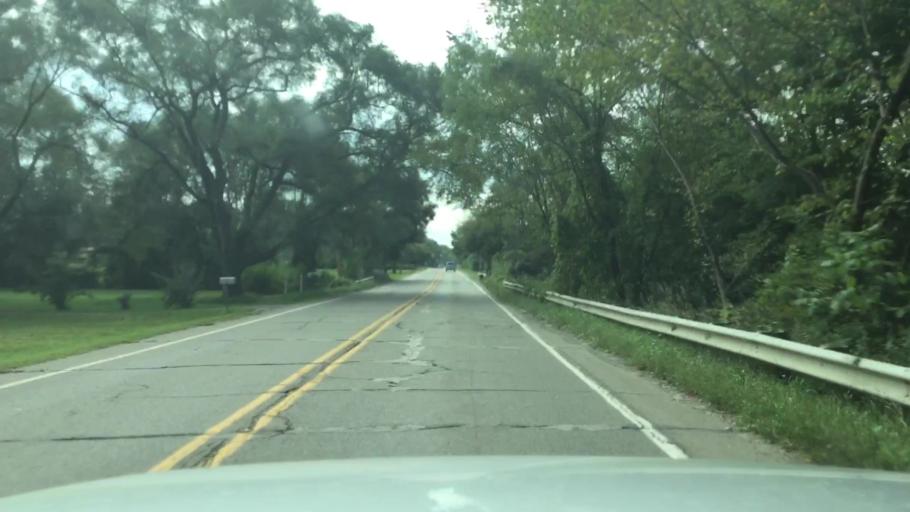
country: US
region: Michigan
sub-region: Wayne County
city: Belleville
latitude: 42.1791
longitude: -83.4830
